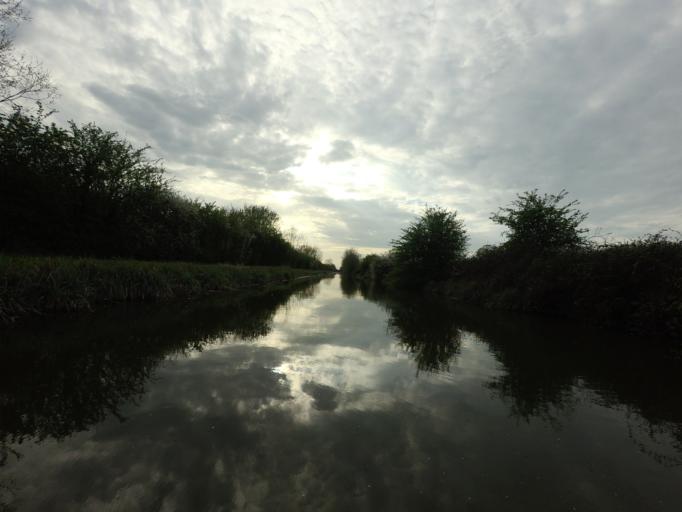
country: GB
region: England
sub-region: Buckinghamshire
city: Aston Clinton
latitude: 51.8173
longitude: -0.7313
